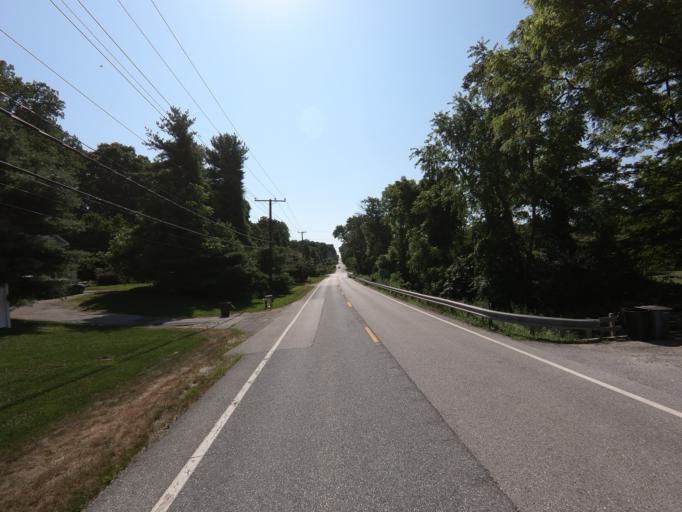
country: US
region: Maryland
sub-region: Carroll County
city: Sykesville
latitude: 39.2978
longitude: -76.9330
